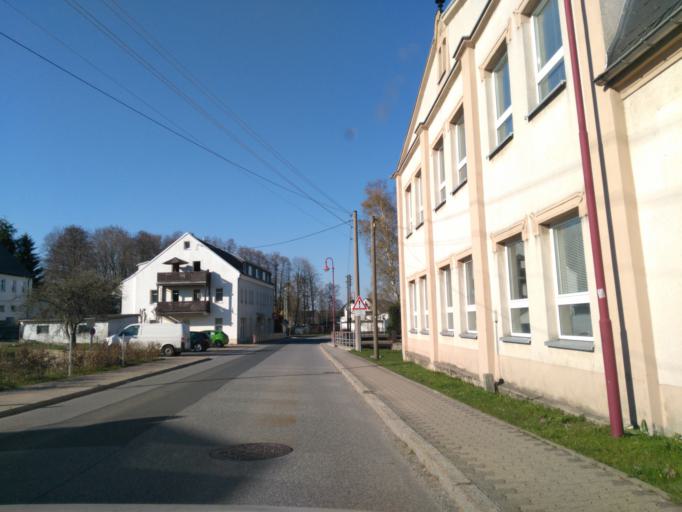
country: DE
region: Saxony
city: Crottendorf
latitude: 50.5095
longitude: 12.9364
